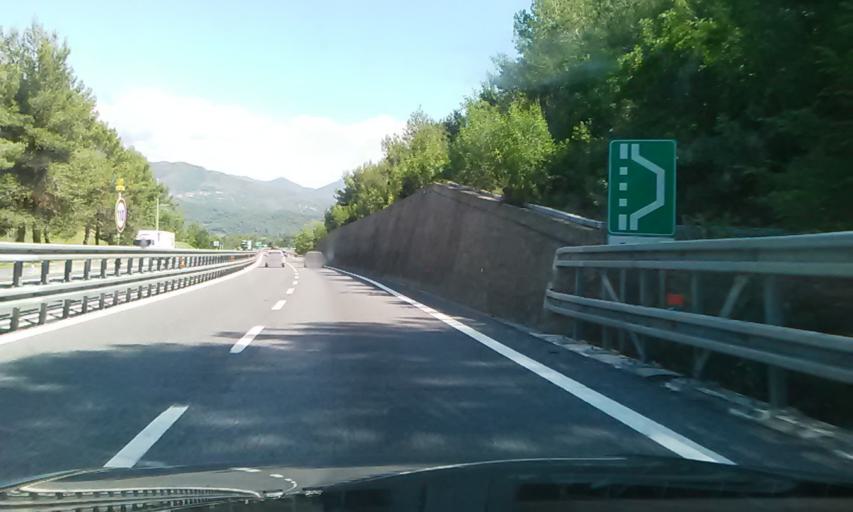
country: IT
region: Liguria
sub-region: Provincia di Savona
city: Villanova d'Albenga
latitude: 44.0335
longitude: 8.1338
